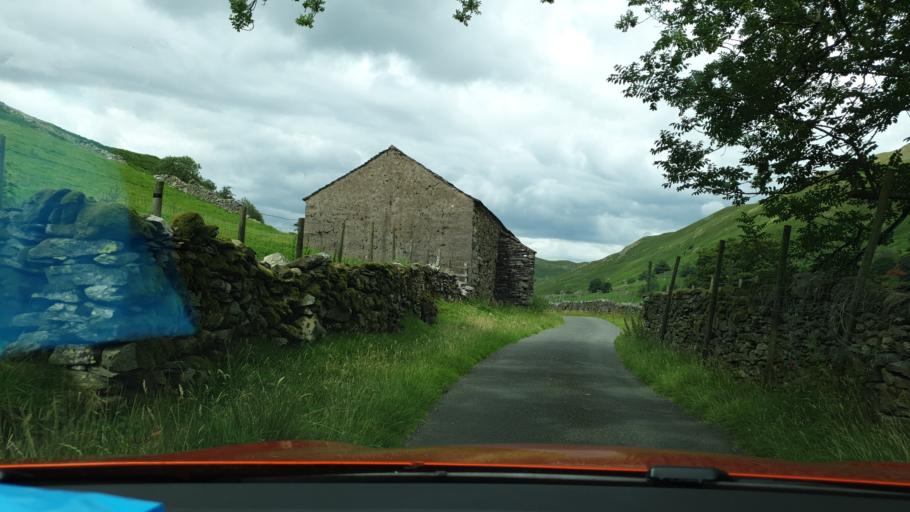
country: GB
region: England
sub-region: Cumbria
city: Ambleside
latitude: 54.5464
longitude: -2.8739
